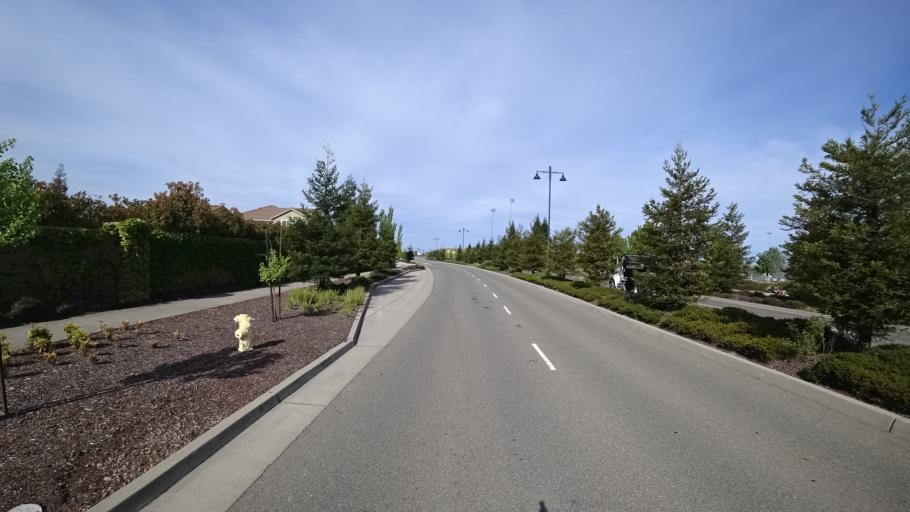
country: US
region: California
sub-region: Placer County
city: Lincoln
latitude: 38.8311
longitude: -121.2847
